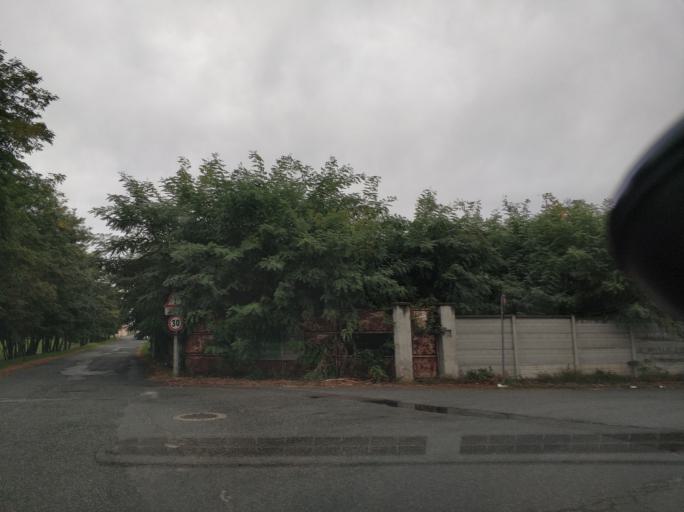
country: IT
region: Piedmont
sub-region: Provincia di Torino
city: Cirie
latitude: 45.2132
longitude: 7.6073
